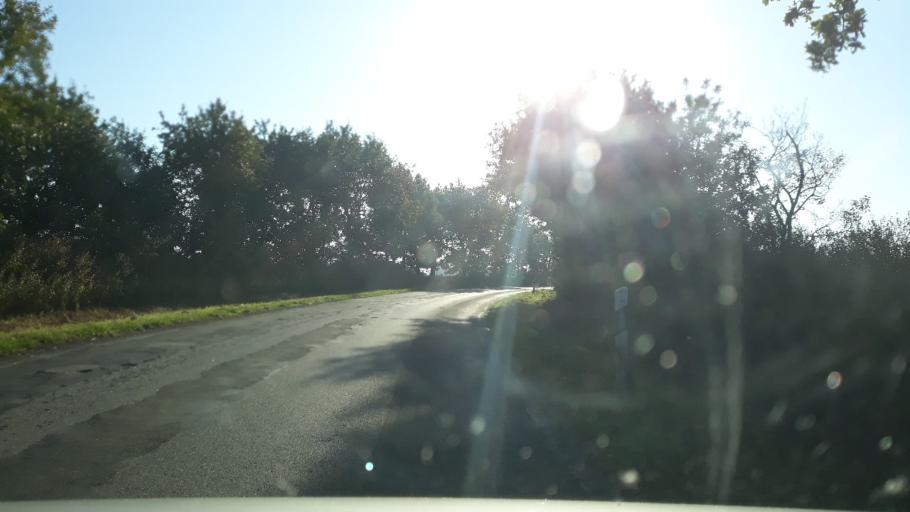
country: DE
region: Schleswig-Holstein
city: Borm
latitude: 54.3982
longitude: 9.3986
